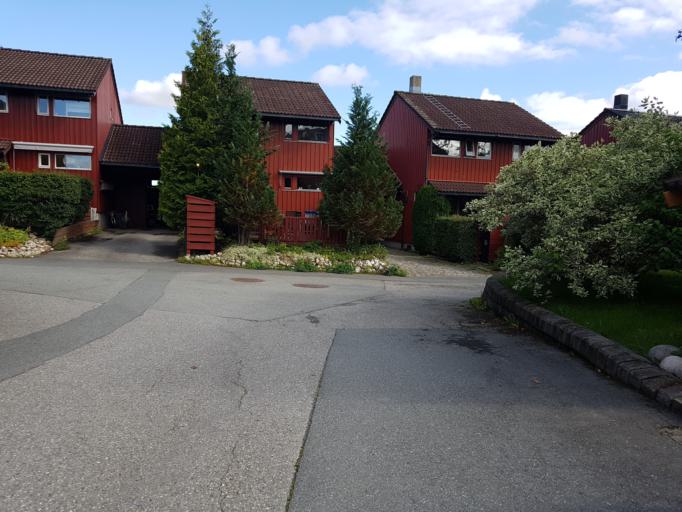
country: NO
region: Sor-Trondelag
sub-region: Trondheim
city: Trondheim
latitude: 63.4168
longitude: 10.4486
